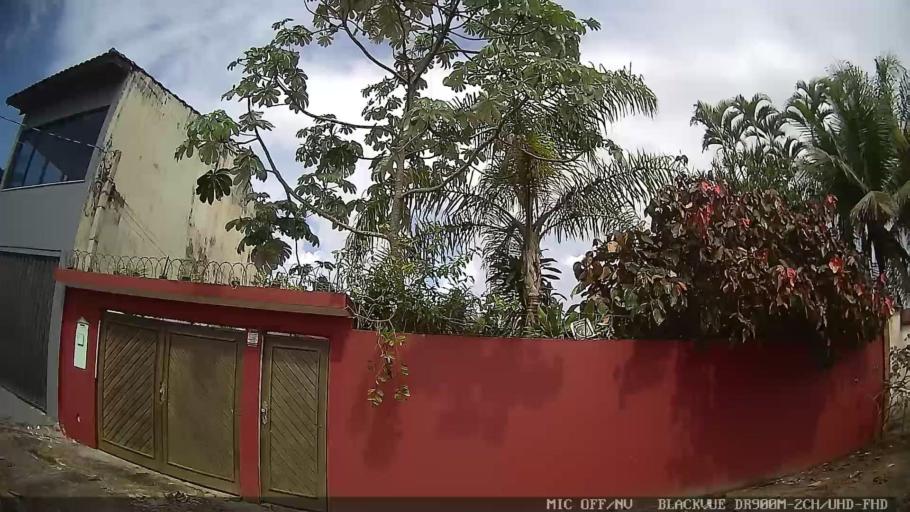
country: BR
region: Sao Paulo
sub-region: Itanhaem
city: Itanhaem
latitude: -24.1442
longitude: -46.7132
